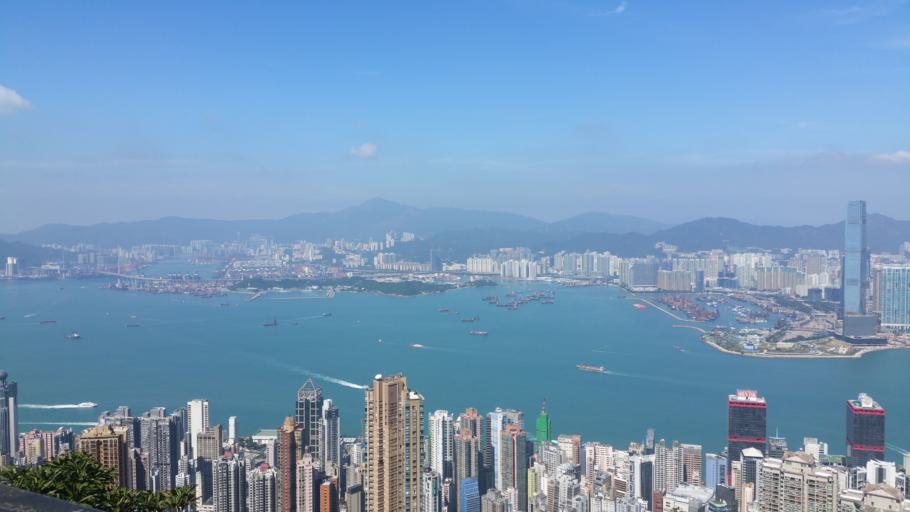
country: HK
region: Central and Western
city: Central
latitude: 22.2777
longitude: 114.1476
